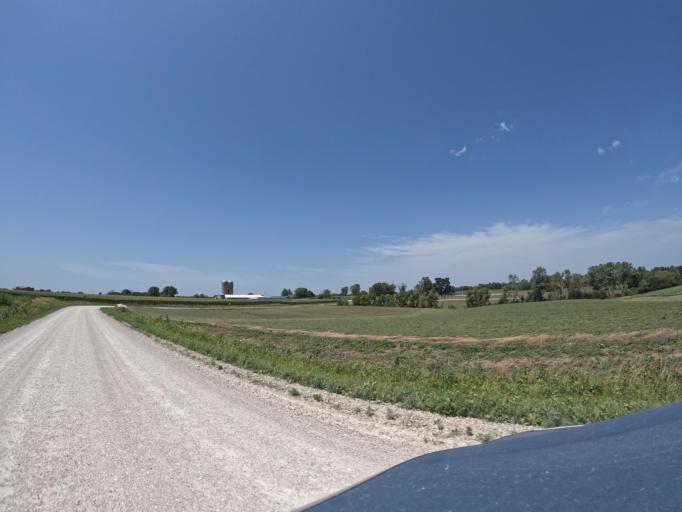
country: US
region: Iowa
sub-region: Henry County
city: Mount Pleasant
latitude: 40.9426
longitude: -91.6544
